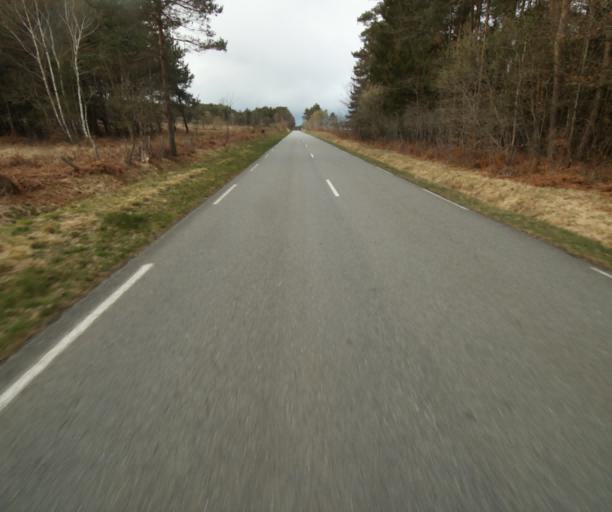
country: FR
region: Limousin
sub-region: Departement de la Correze
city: Saint-Privat
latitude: 45.2028
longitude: 2.0046
